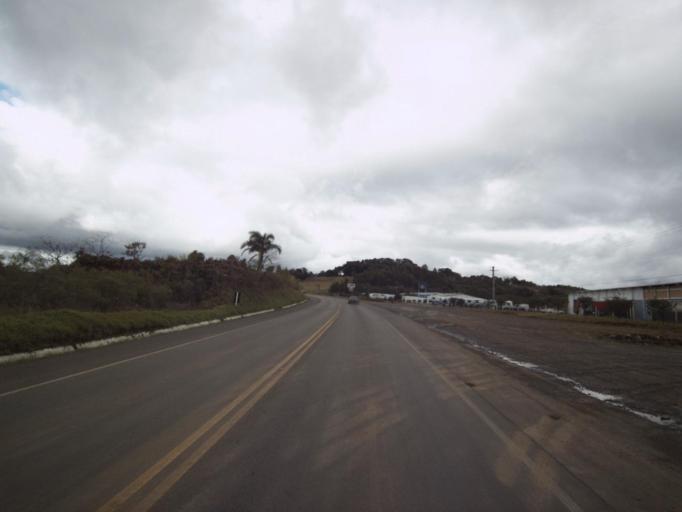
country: BR
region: Santa Catarina
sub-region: Concordia
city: Concordia
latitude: -27.2554
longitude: -51.9542
